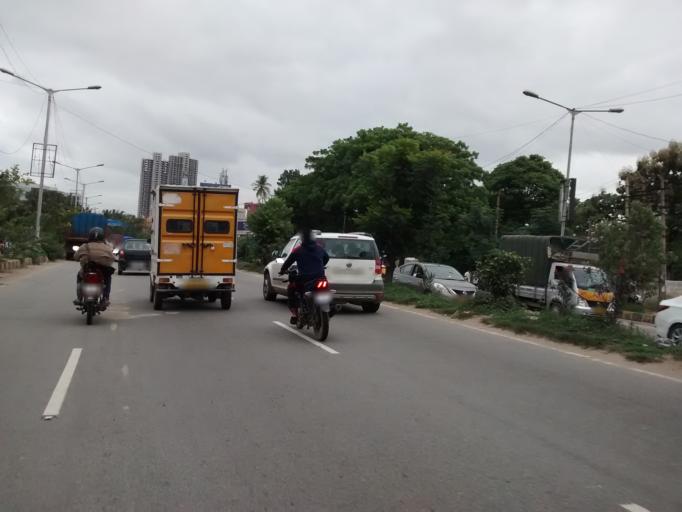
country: IN
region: Karnataka
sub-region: Bangalore Urban
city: Yelahanka
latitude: 13.0410
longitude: 77.6191
